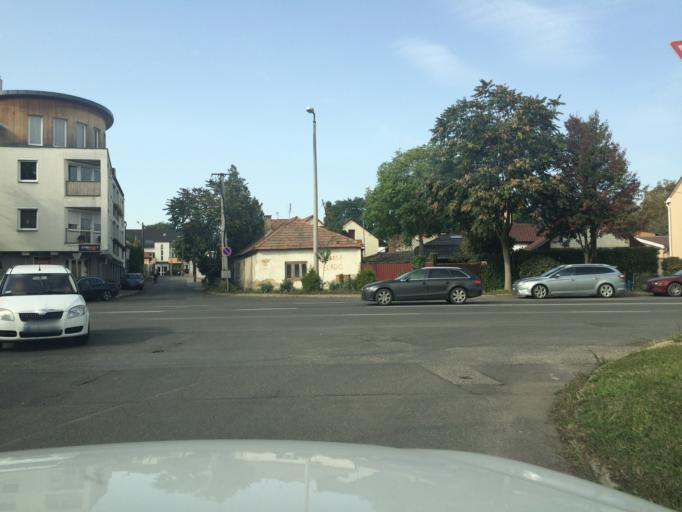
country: HU
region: Szabolcs-Szatmar-Bereg
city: Nyiregyhaza
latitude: 47.9610
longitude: 21.7227
